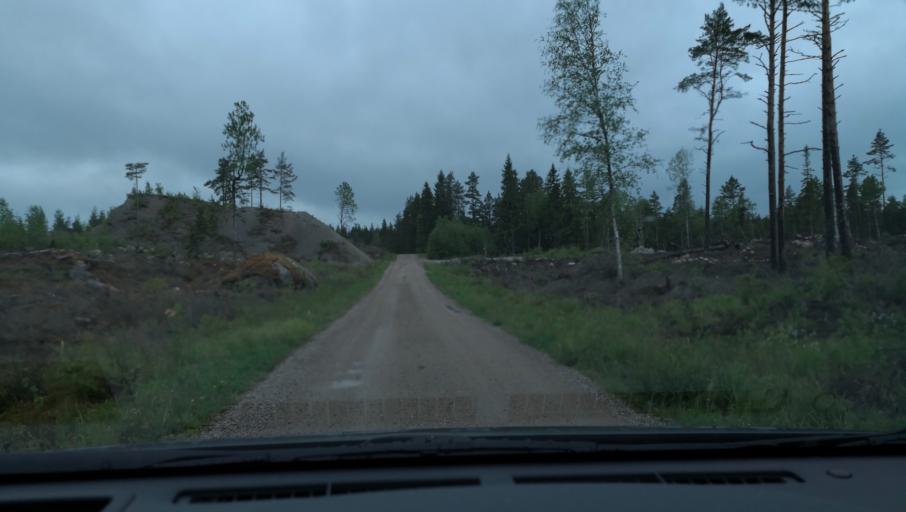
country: SE
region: Uppsala
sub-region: Enkopings Kommun
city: Orsundsbro
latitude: 59.9408
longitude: 17.3121
